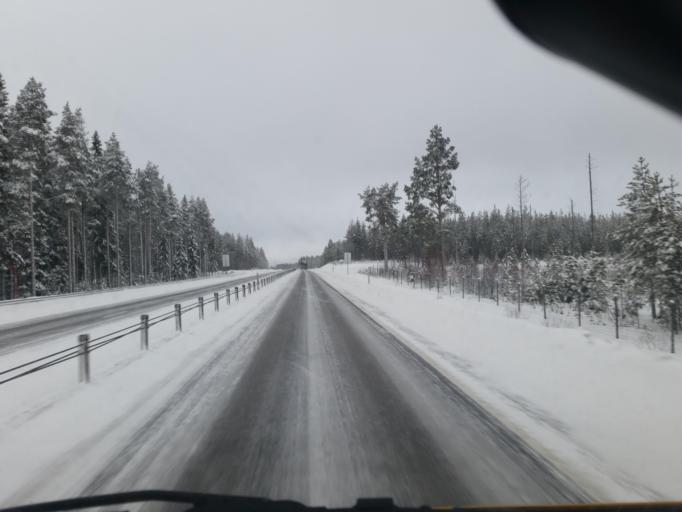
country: SE
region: Norrbotten
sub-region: Pitea Kommun
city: Pitea
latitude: 65.2699
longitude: 21.4570
